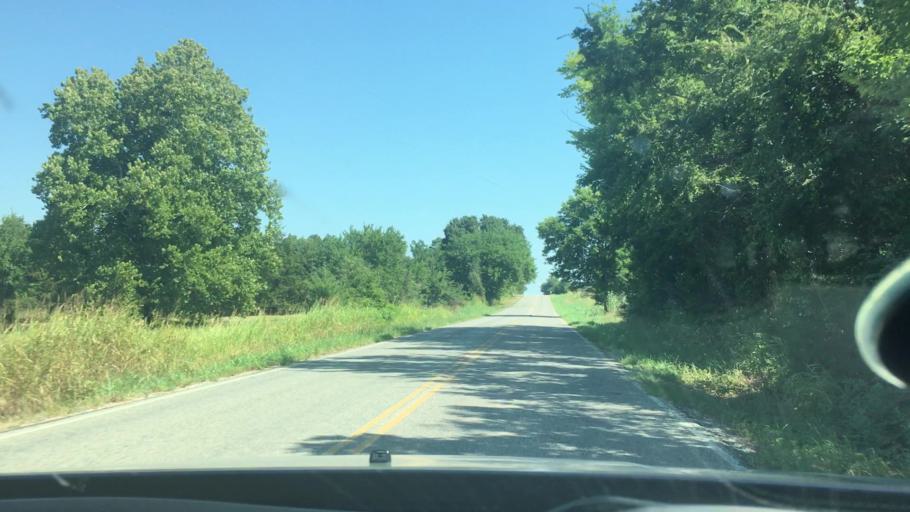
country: US
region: Oklahoma
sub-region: Johnston County
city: Tishomingo
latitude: 34.2568
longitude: -96.6186
